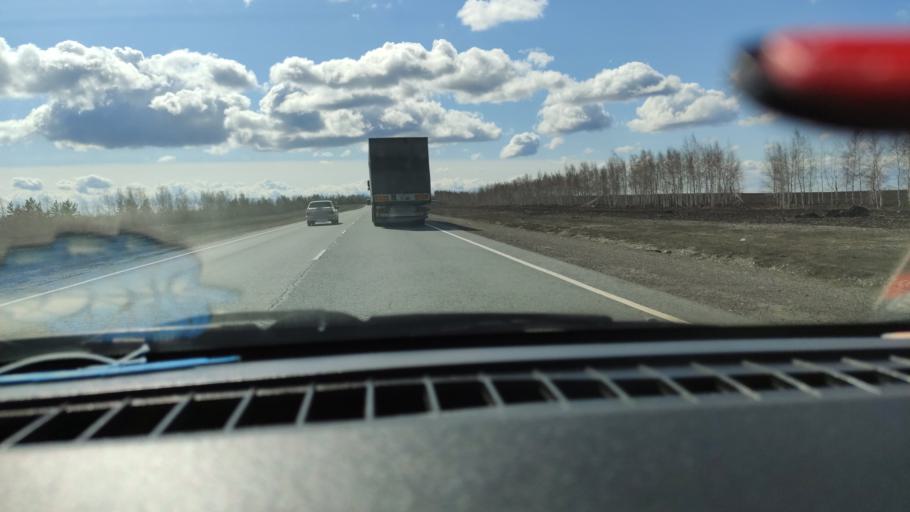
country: RU
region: Samara
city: Syzran'
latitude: 52.9376
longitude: 48.3073
